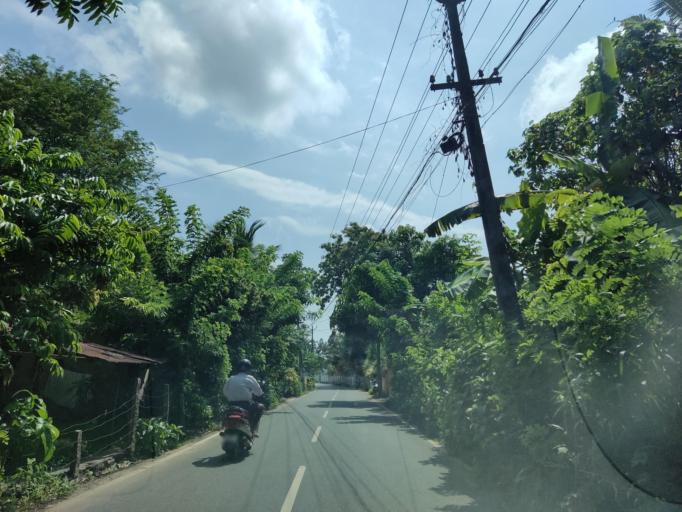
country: IN
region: Kerala
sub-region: Alappuzha
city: Mavelikara
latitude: 9.3235
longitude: 76.5252
